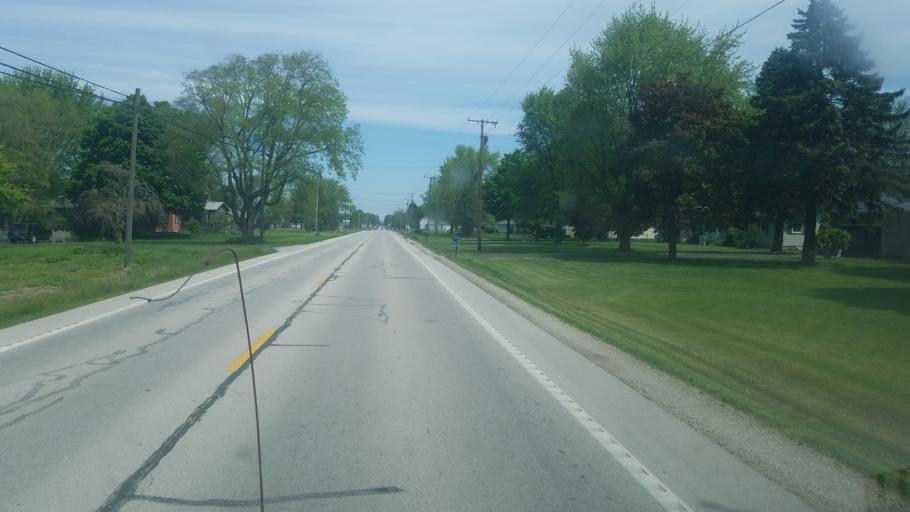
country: US
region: Ohio
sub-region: Seneca County
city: Tiffin
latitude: 41.1973
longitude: -83.1678
